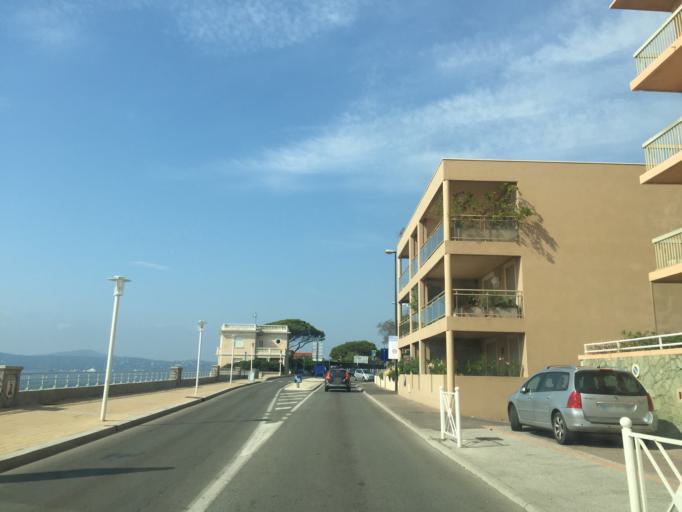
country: FR
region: Provence-Alpes-Cote d'Azur
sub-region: Departement du Var
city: Sainte-Maxime
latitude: 43.3063
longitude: 6.6328
